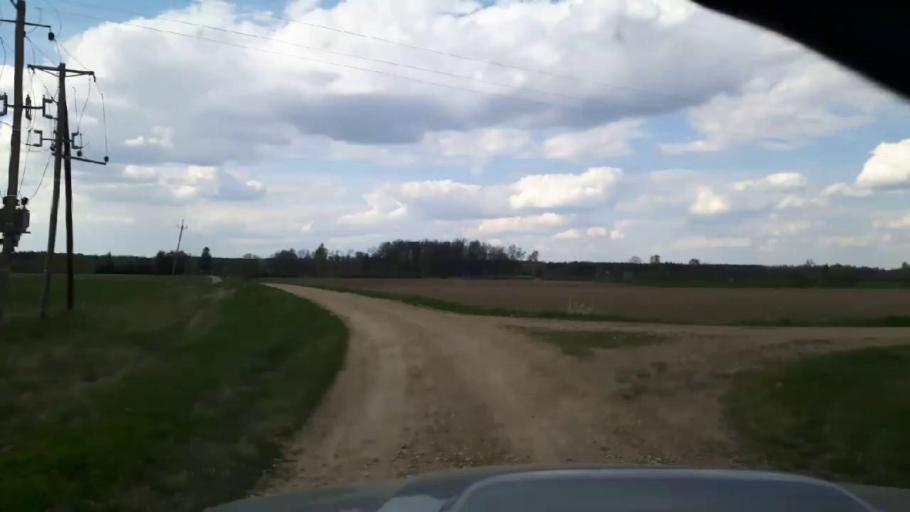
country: EE
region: Paernumaa
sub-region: Sindi linn
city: Sindi
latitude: 58.4336
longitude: 24.7378
